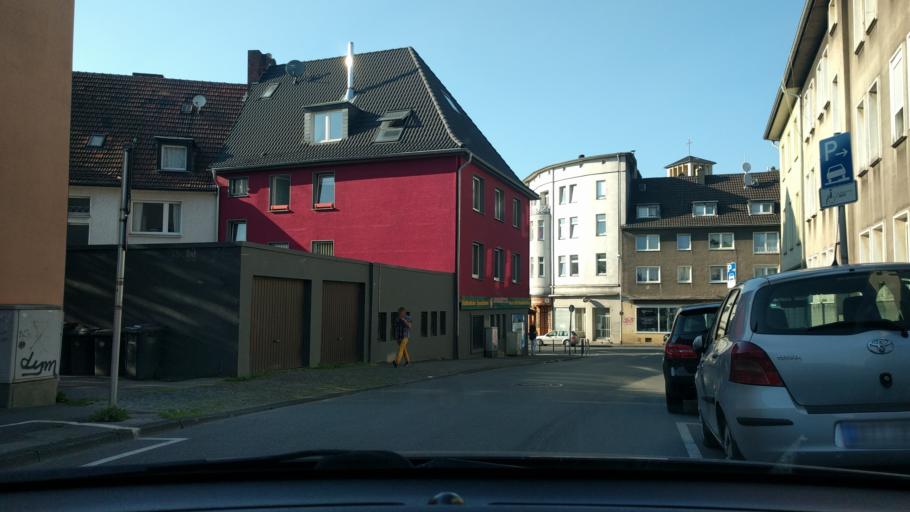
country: DE
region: North Rhine-Westphalia
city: Witten
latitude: 51.4397
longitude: 7.3390
